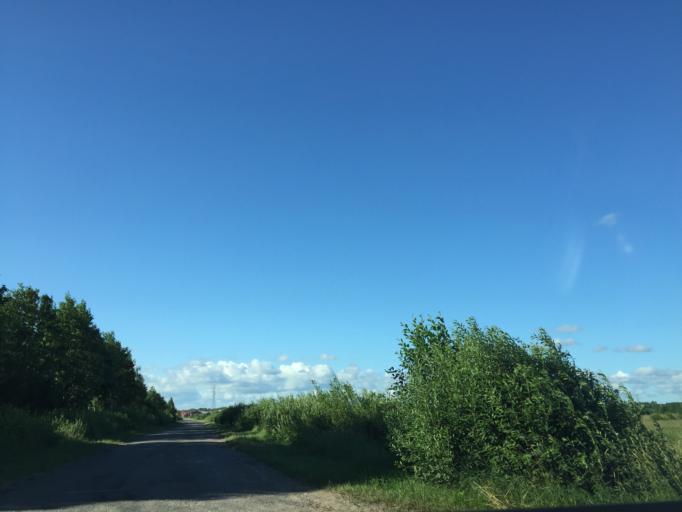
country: LV
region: Ventspils
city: Ventspils
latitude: 57.4057
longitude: 21.6479
